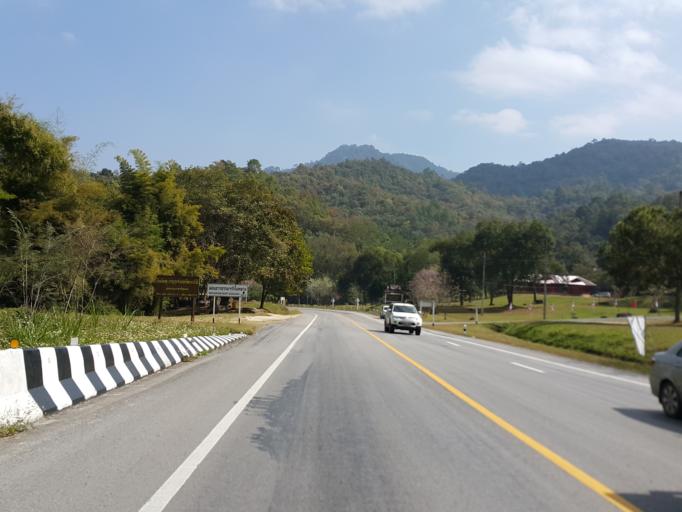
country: TH
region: Lampang
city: Wang Nuea
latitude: 19.0784
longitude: 99.3971
